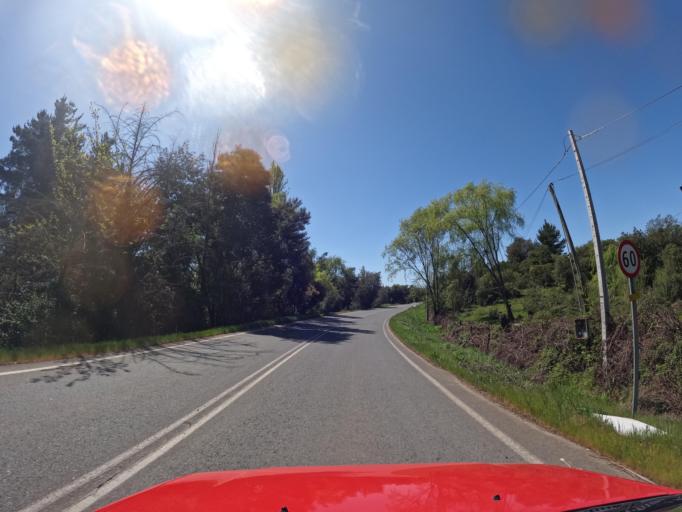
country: CL
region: Maule
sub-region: Provincia de Talca
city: San Clemente
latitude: -35.4830
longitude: -71.2713
